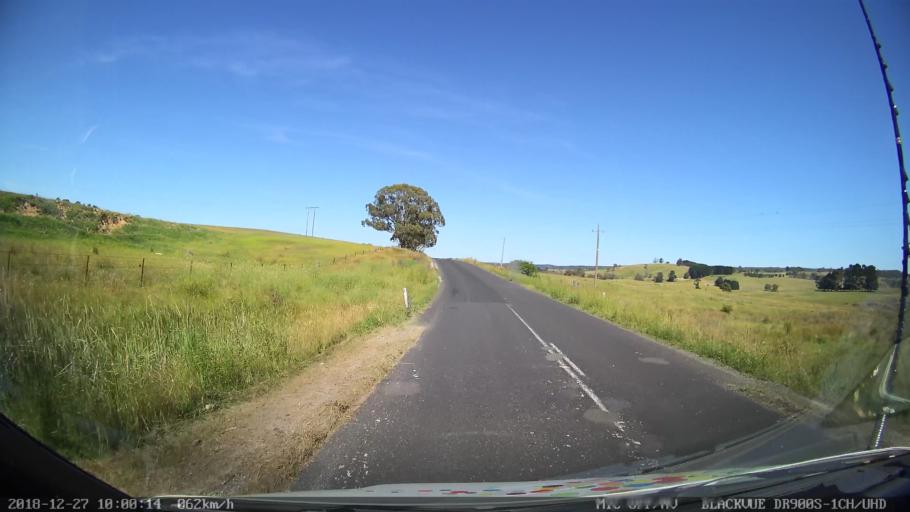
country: AU
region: New South Wales
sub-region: Lithgow
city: Portland
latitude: -33.4367
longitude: 149.9431
